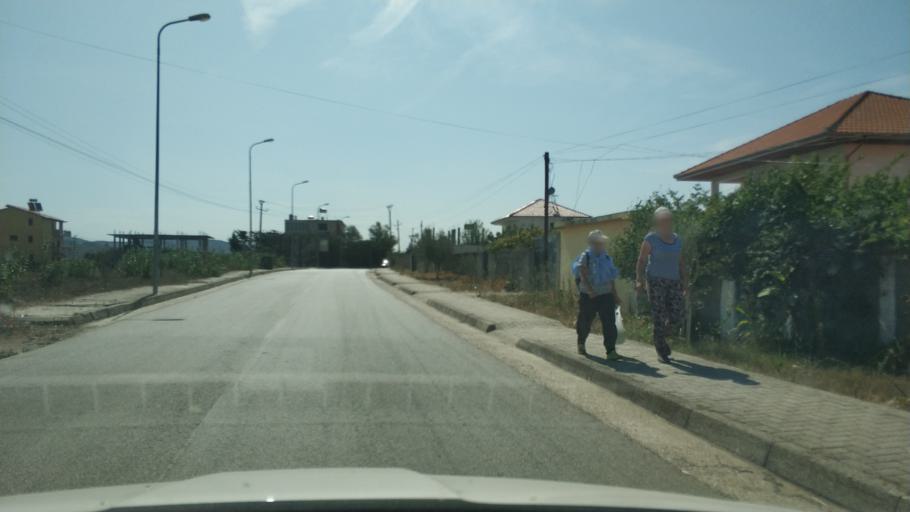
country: AL
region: Fier
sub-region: Rrethi i Lushnjes
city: Divjake
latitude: 40.9892
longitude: 19.5342
